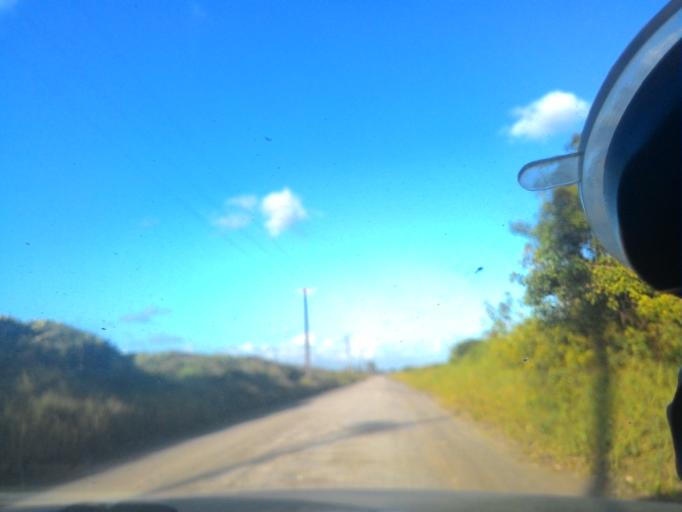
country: BR
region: Sao Paulo
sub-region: Pariquera-Acu
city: Pariquera Acu
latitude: -24.8750
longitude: -47.7283
